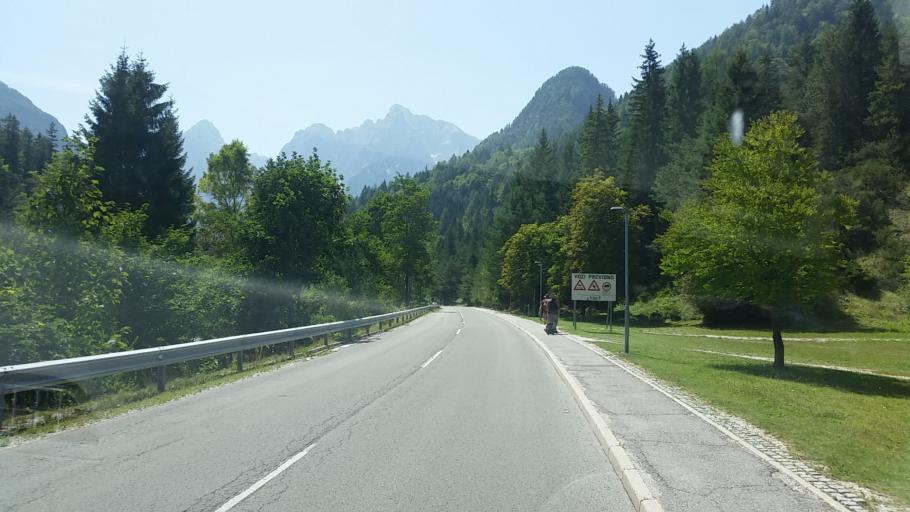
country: SI
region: Kranjska Gora
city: Kranjska Gora
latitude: 46.4800
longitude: 13.7808
